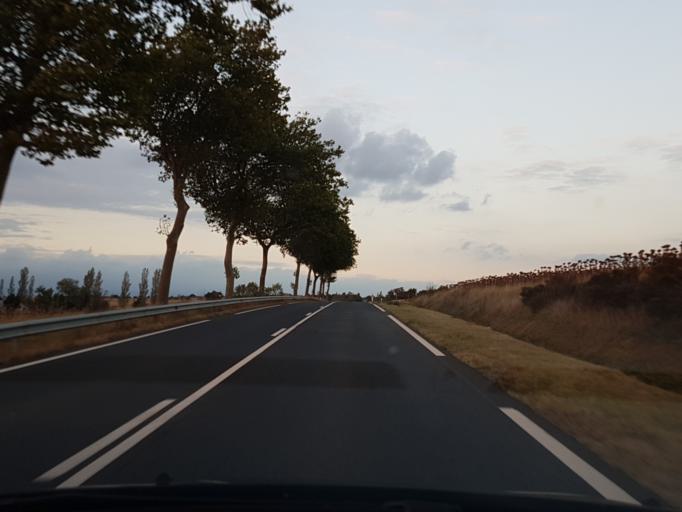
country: FR
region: Languedoc-Roussillon
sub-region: Departement de l'Aude
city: Saint-Martin-Lalande
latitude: 43.1720
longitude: 2.0047
